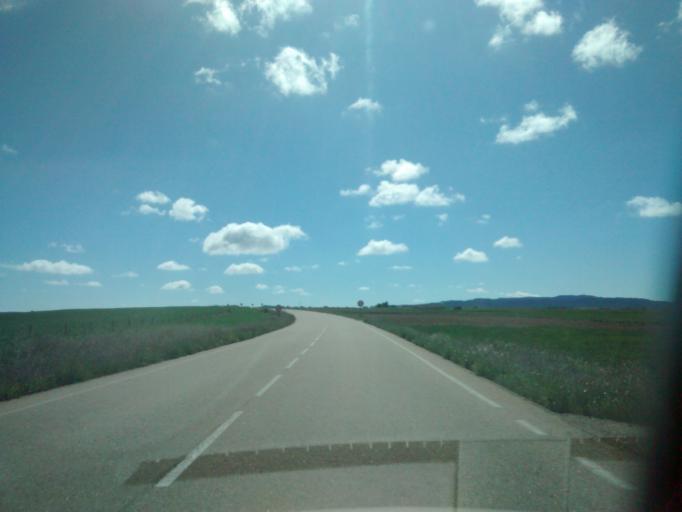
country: ES
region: Aragon
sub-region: Provincia de Zaragoza
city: Lecinena
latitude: 41.7972
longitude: -0.6556
